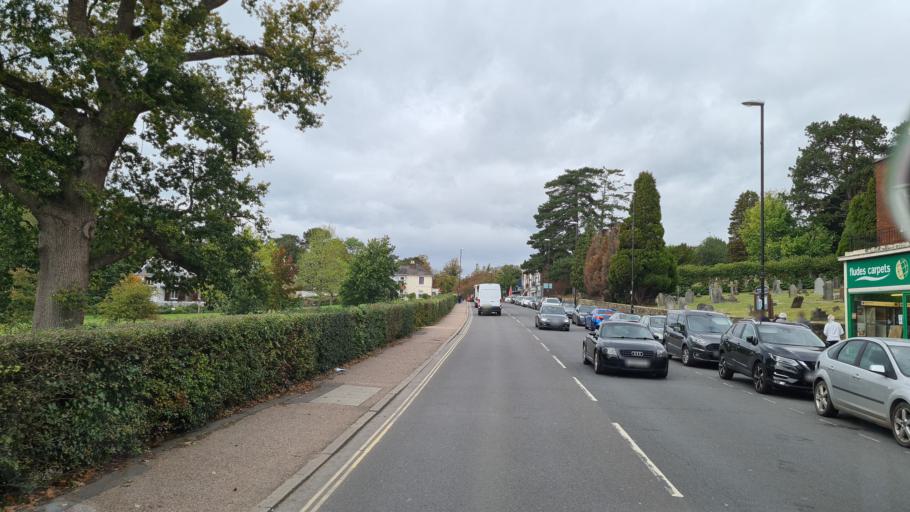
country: GB
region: England
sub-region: West Sussex
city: Haywards Heath
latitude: 50.9980
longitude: -0.1042
